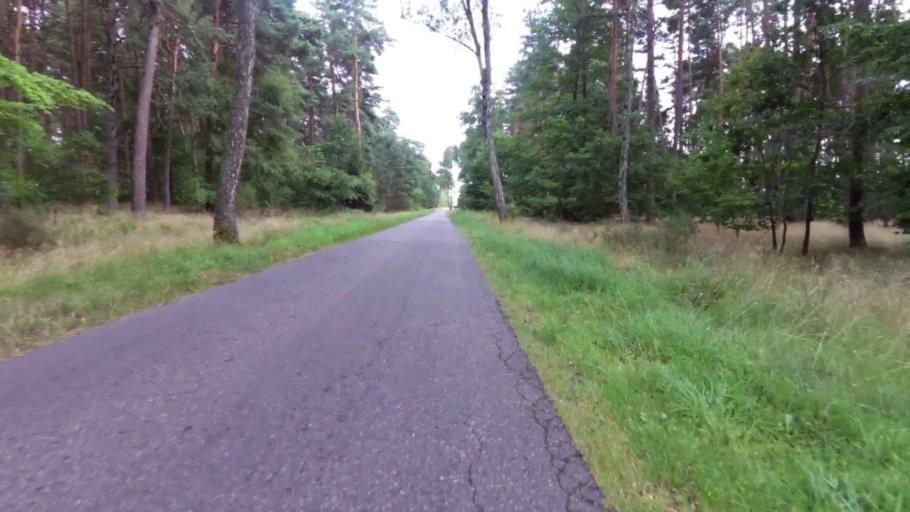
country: PL
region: West Pomeranian Voivodeship
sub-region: Powiat drawski
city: Zlocieniec
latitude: 53.5508
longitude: 15.9941
